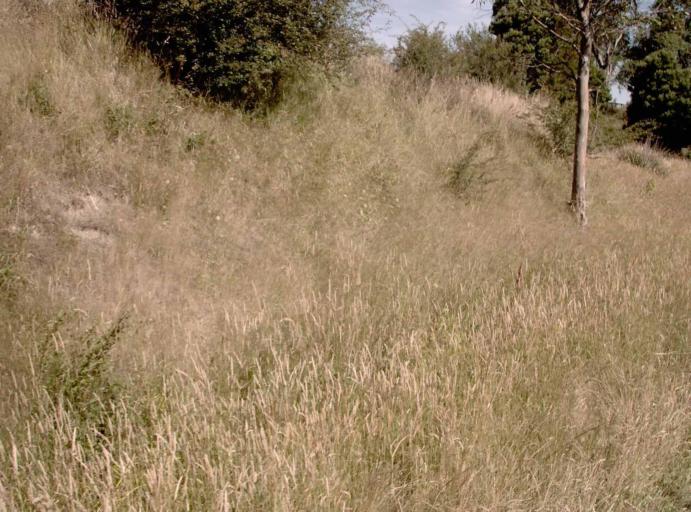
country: AU
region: Victoria
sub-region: Baw Baw
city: Warragul
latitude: -38.3218
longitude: 145.7692
